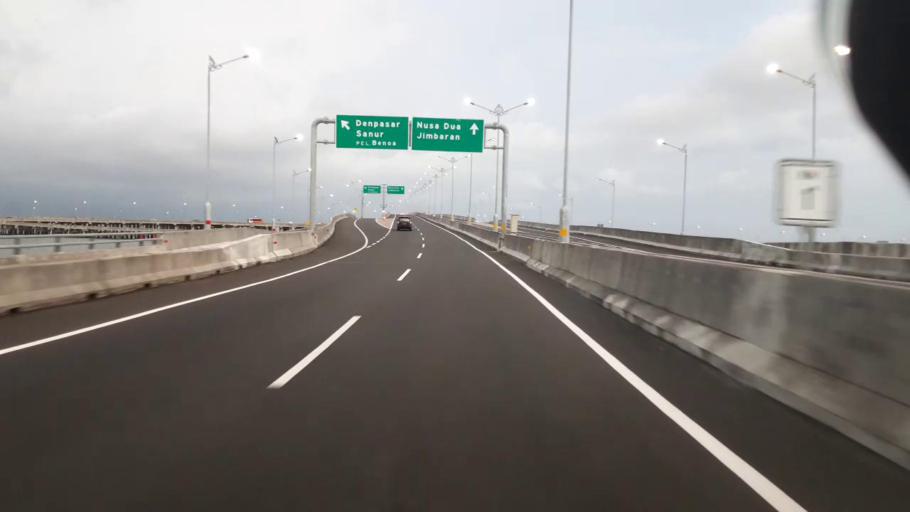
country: ID
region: Bali
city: Kelanabian
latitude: -8.7446
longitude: 115.1925
